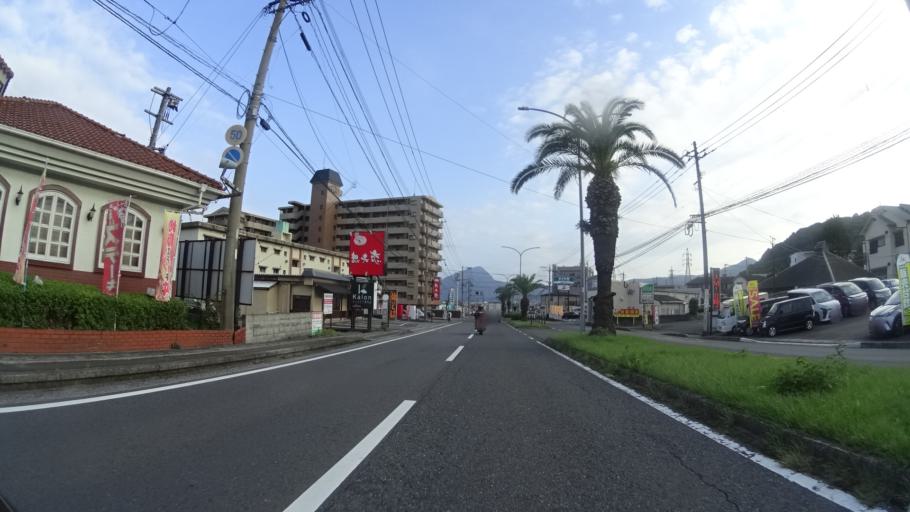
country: JP
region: Oita
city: Beppu
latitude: 33.3080
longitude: 131.4880
